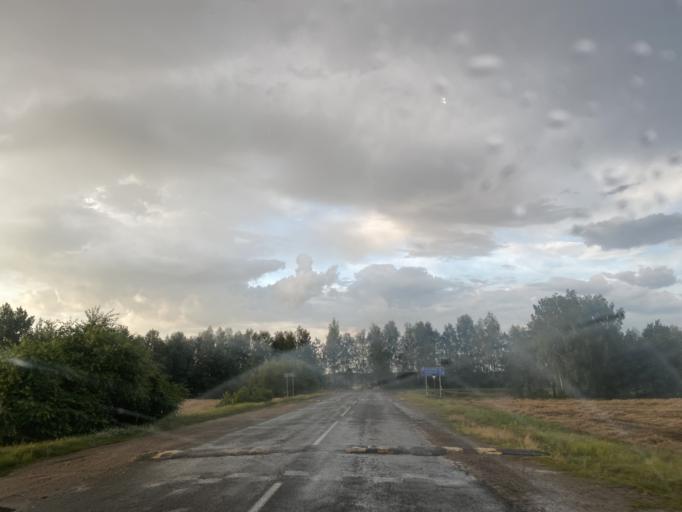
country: BY
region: Brest
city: Tsyelyakhany
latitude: 52.5578
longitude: 25.6396
